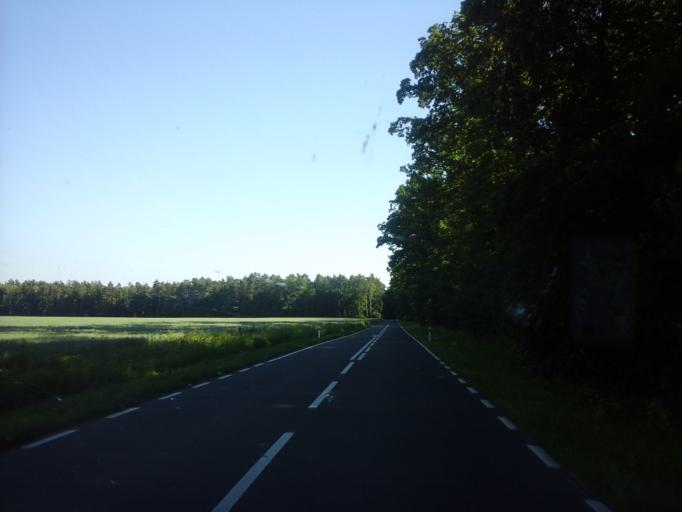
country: PL
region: West Pomeranian Voivodeship
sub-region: Powiat stargardzki
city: Chociwel
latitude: 53.4991
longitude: 15.3398
